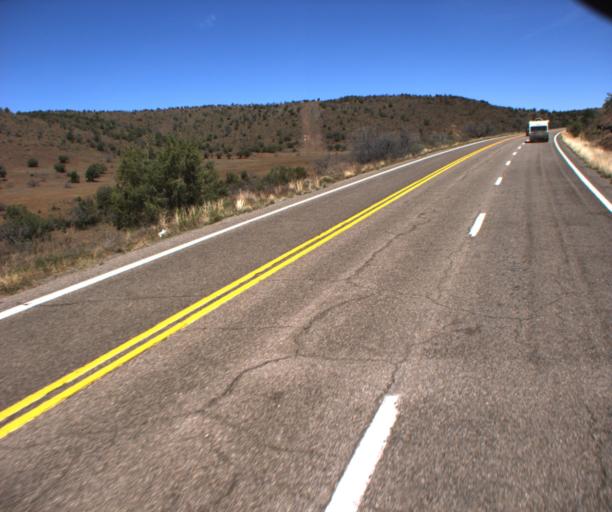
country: US
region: Arizona
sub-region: Mohave County
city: Peach Springs
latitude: 35.4408
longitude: -113.6446
